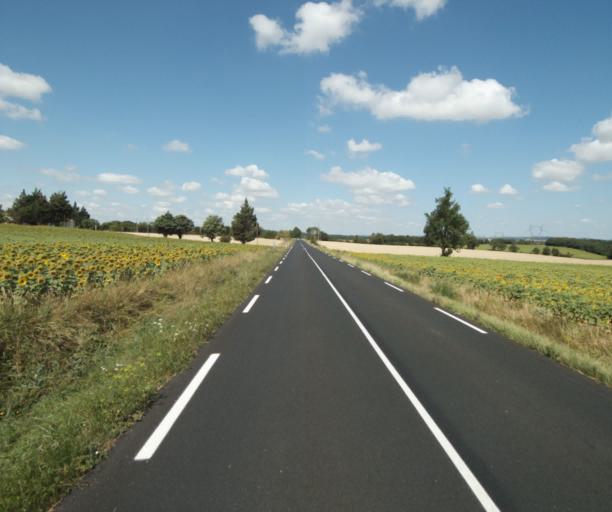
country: FR
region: Midi-Pyrenees
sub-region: Departement de la Haute-Garonne
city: Auriac-sur-Vendinelle
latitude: 43.4642
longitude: 1.8124
